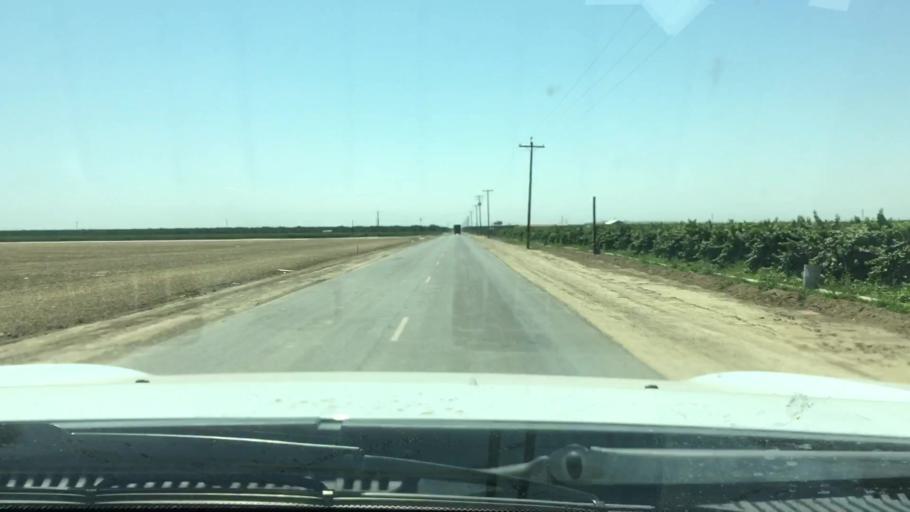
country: US
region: California
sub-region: Kern County
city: Wasco
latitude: 35.5358
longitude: -119.4032
